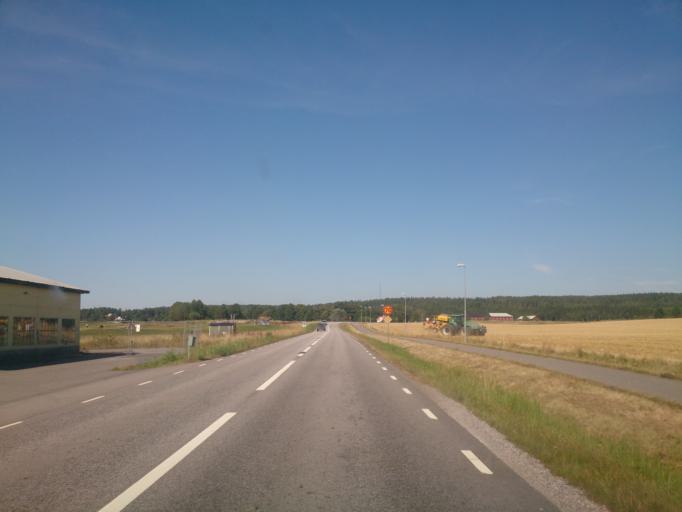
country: SE
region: OEstergoetland
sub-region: Norrkopings Kommun
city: Norrkoping
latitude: 58.4897
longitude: 16.1751
